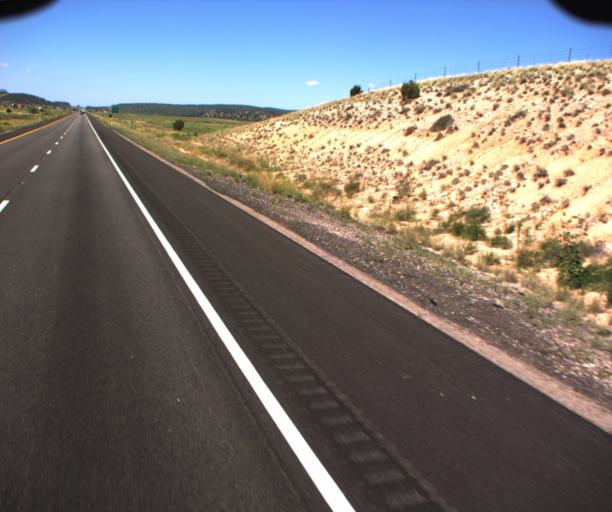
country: US
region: Arizona
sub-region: Mohave County
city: Peach Springs
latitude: 35.2639
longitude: -113.1576
